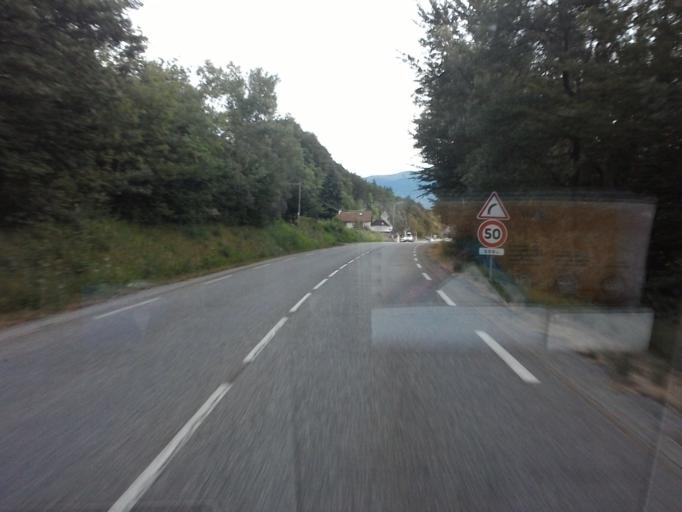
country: FR
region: Provence-Alpes-Cote d'Azur
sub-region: Departement des Hautes-Alpes
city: Saint-Bonnet-en-Champsaur
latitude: 44.7329
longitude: 6.0044
